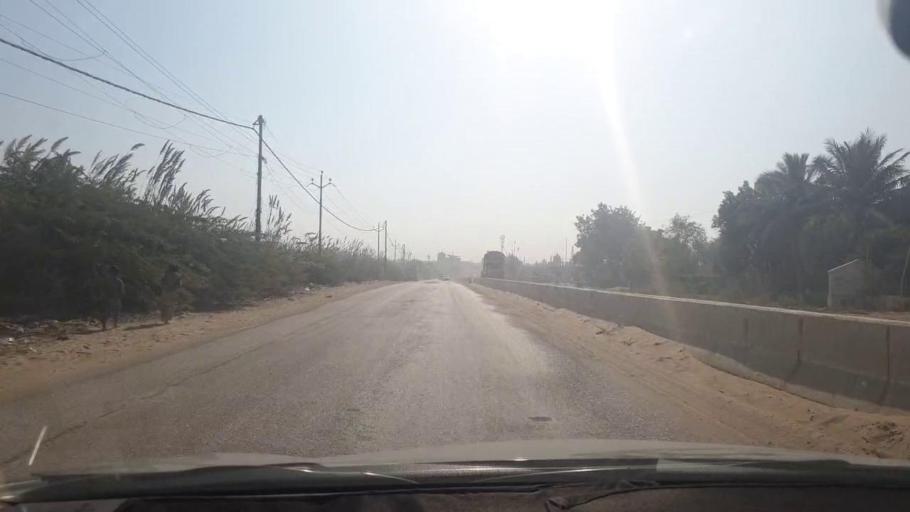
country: PK
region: Sindh
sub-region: Karachi District
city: Karachi
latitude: 25.0035
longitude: 67.0339
